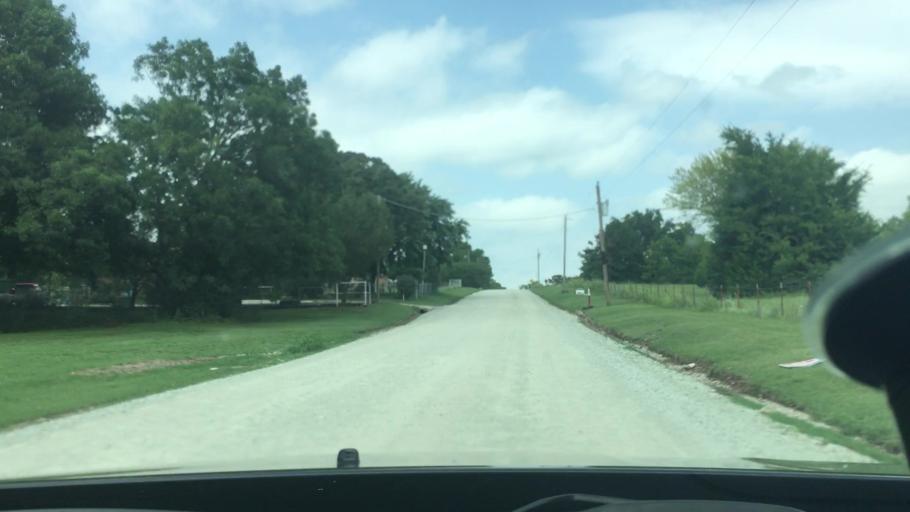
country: US
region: Oklahoma
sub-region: Pontotoc County
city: Ada
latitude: 34.8148
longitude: -96.7572
